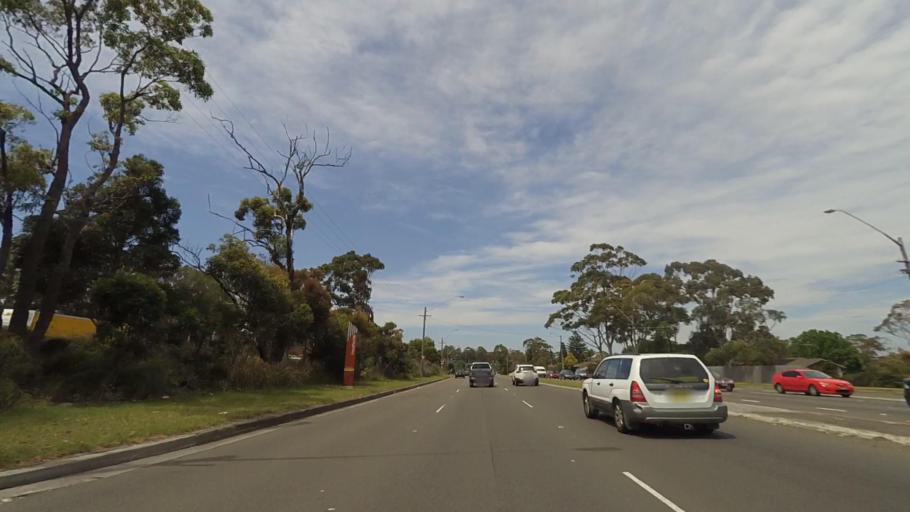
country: AU
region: New South Wales
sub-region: Sutherland Shire
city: Heathcote
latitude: -34.0796
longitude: 151.0108
